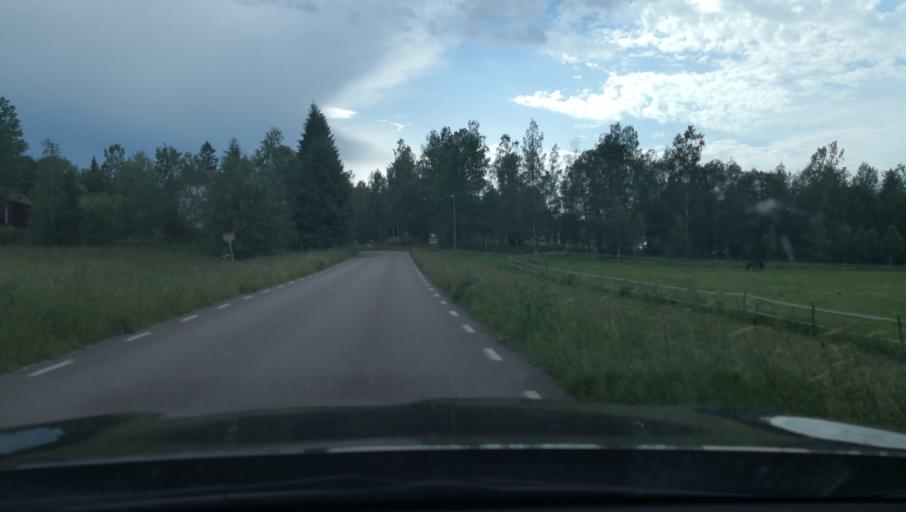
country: SE
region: Dalarna
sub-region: Smedjebackens Kommun
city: Smedjebacken
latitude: 60.0489
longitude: 15.5293
